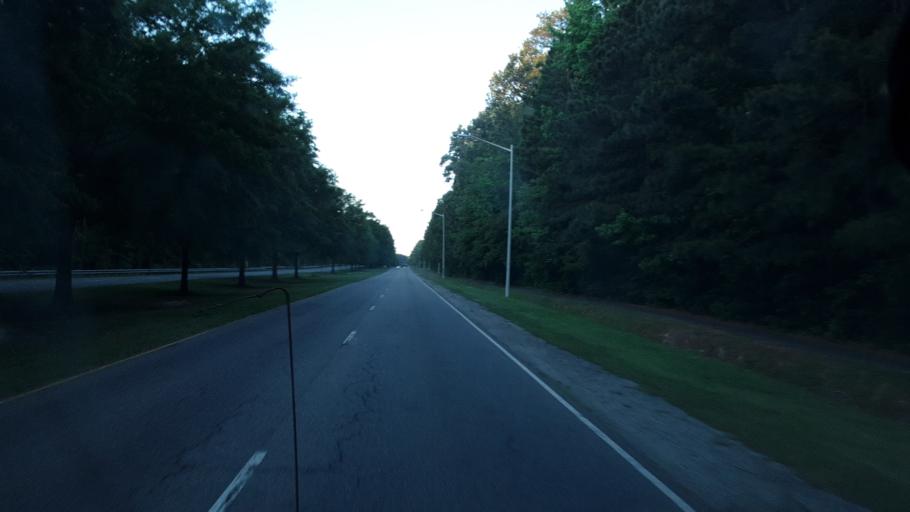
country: US
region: Virginia
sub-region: City of Virginia Beach
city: Virginia Beach
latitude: 36.8043
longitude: -75.9921
